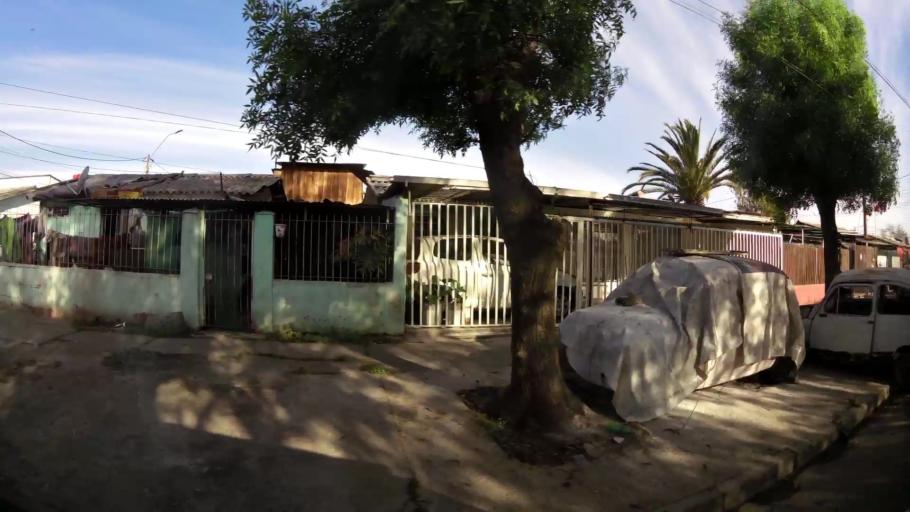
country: CL
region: Santiago Metropolitan
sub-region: Provincia de Santiago
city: Lo Prado
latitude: -33.4777
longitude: -70.7013
